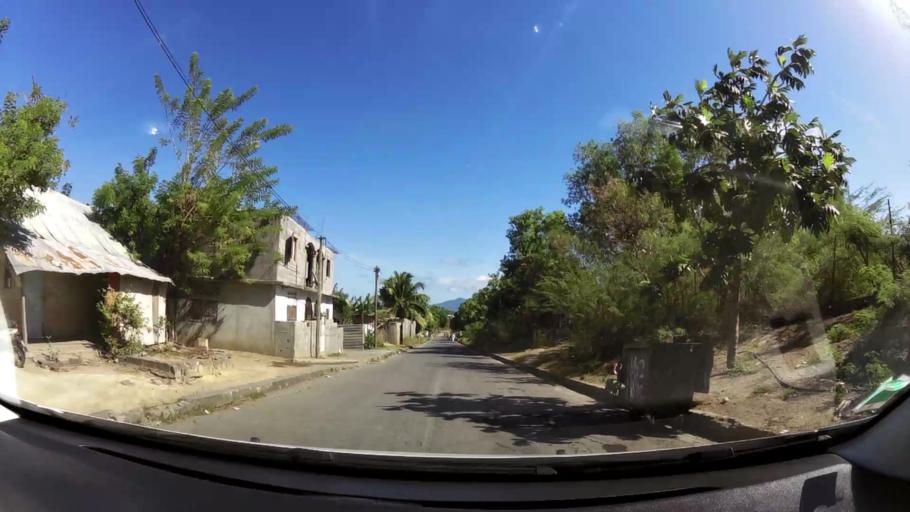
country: YT
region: Pamandzi
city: Pamandzi
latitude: -12.7827
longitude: 45.2765
